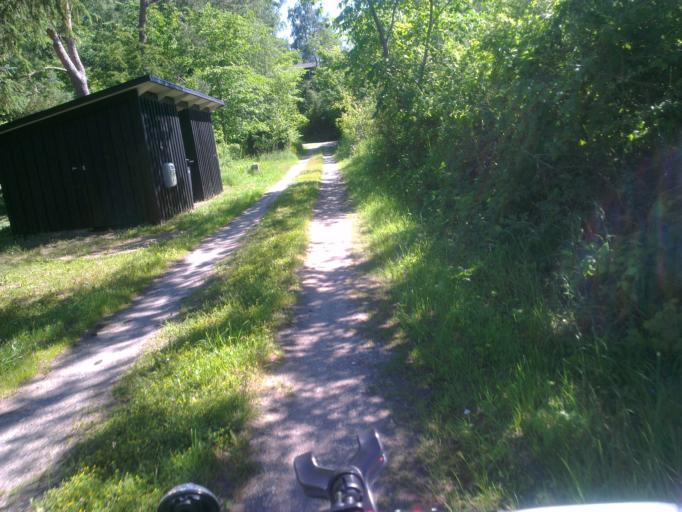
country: DK
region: Capital Region
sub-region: Halsnaes Kommune
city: Liseleje
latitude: 55.9319
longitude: 11.9384
